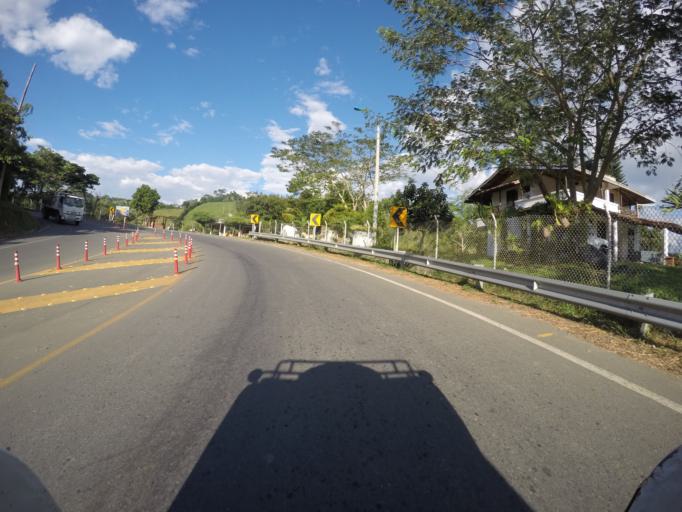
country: CO
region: Valle del Cauca
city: Alcala
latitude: 4.7025
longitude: -75.8497
